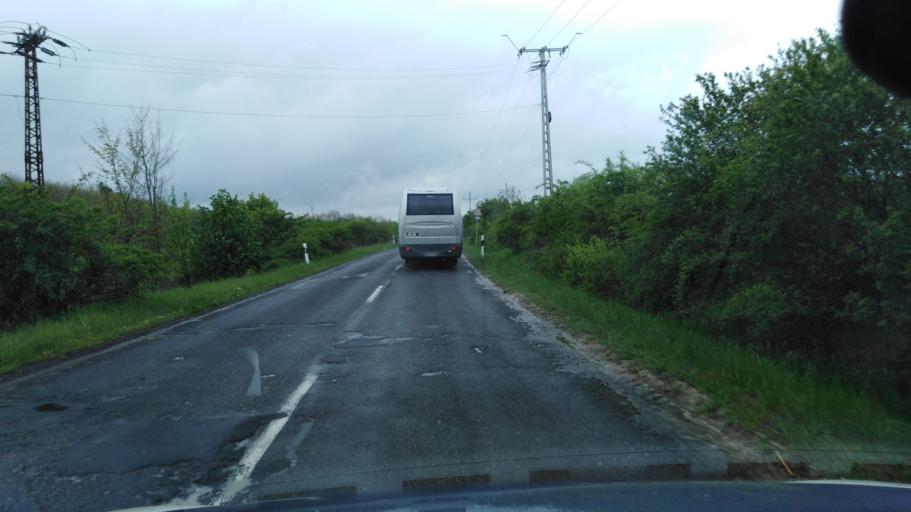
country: HU
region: Nograd
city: Rimoc
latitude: 48.0119
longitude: 19.6001
